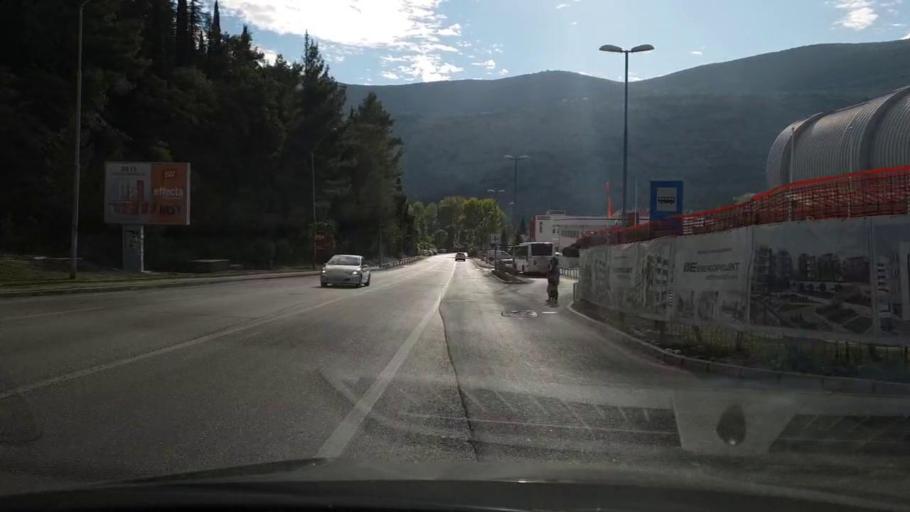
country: ME
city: Igalo
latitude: 42.4579
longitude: 18.5064
